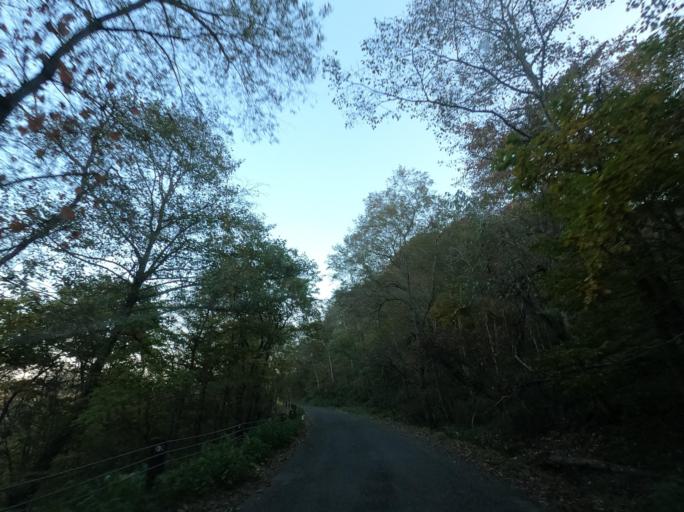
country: JP
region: Hokkaido
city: Kushiro
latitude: 43.1939
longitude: 144.4637
